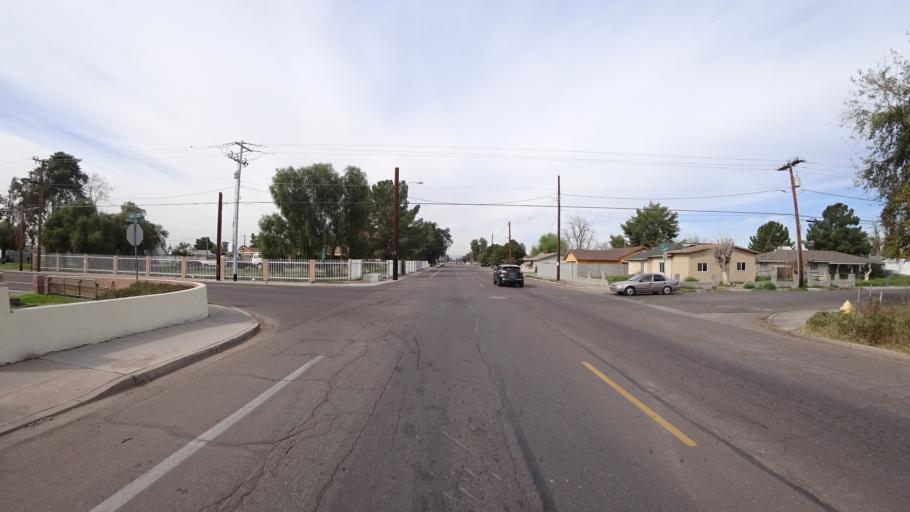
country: US
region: Arizona
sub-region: Maricopa County
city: Glendale
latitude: 33.5312
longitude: -112.1906
